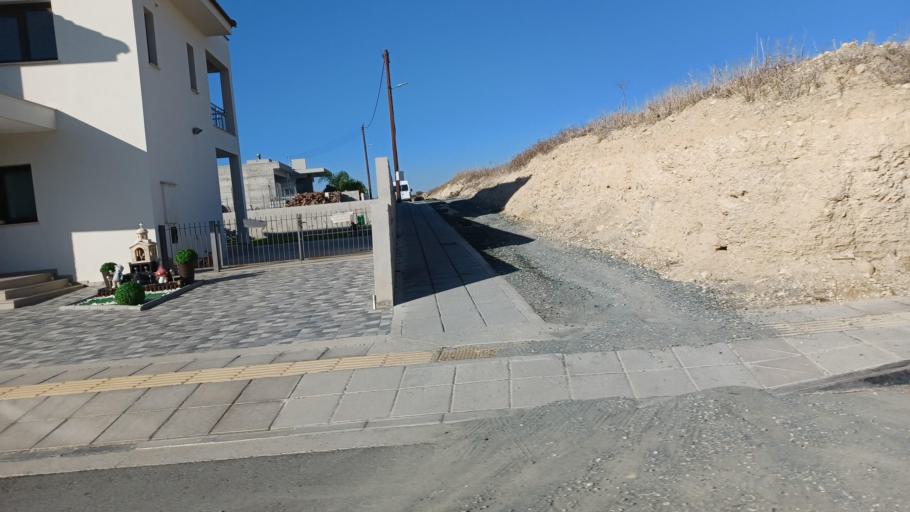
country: CY
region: Larnaka
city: Athienou
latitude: 35.0624
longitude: 33.5281
